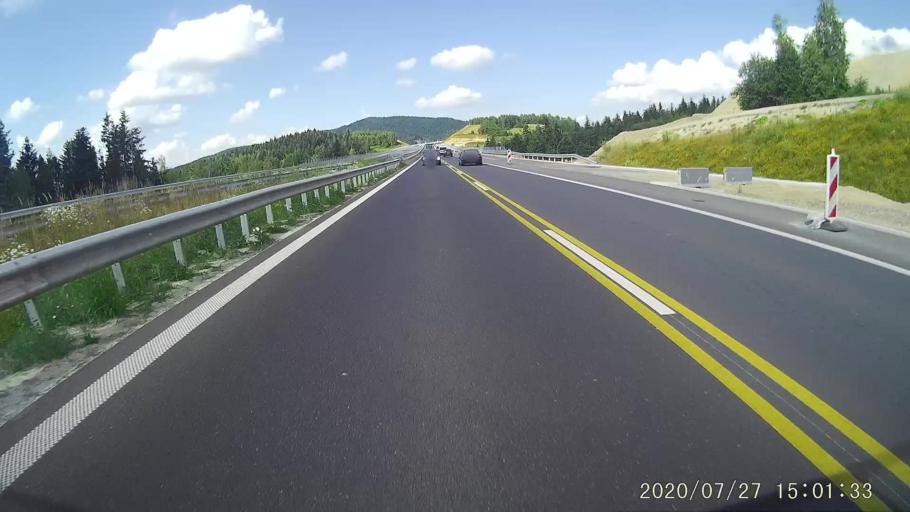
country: PL
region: Lesser Poland Voivodeship
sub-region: Powiat suski
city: Letownia
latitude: 49.6815
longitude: 19.8911
